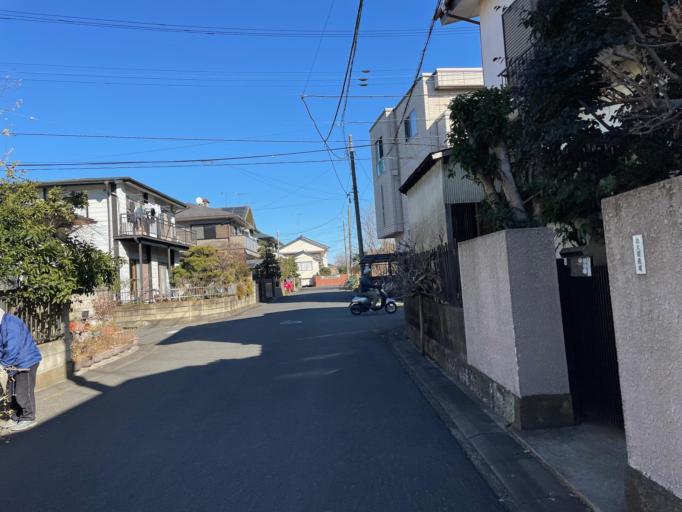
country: JP
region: Saitama
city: Ageoshimo
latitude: 35.9691
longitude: 139.6275
